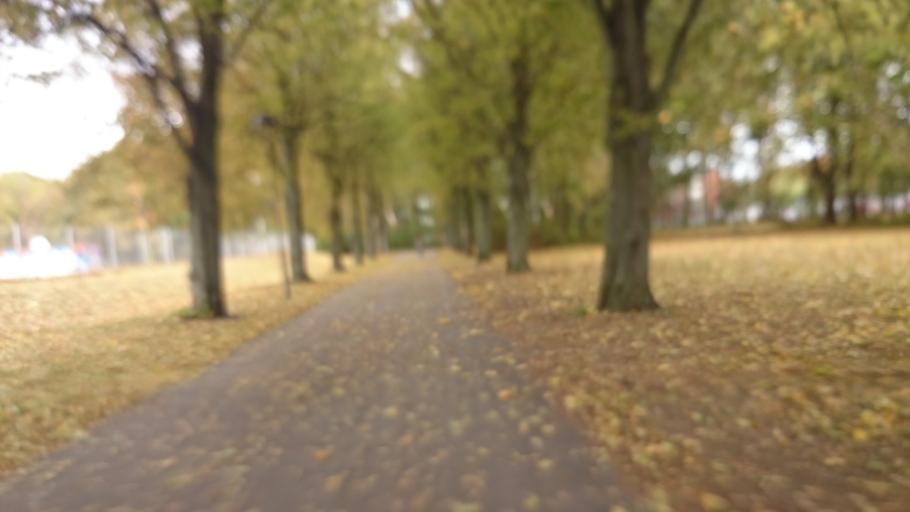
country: SE
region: Skane
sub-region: Lunds Kommun
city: Lund
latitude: 55.7111
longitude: 13.1634
